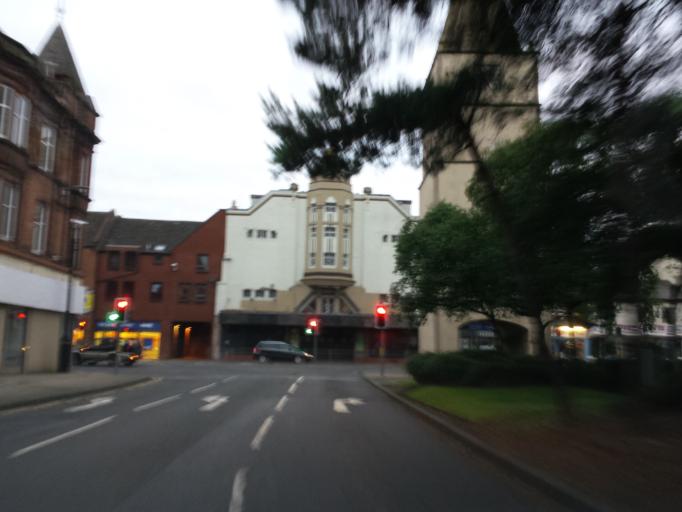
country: GB
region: Scotland
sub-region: South Ayrshire
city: Ayr
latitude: 55.4668
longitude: -4.6297
